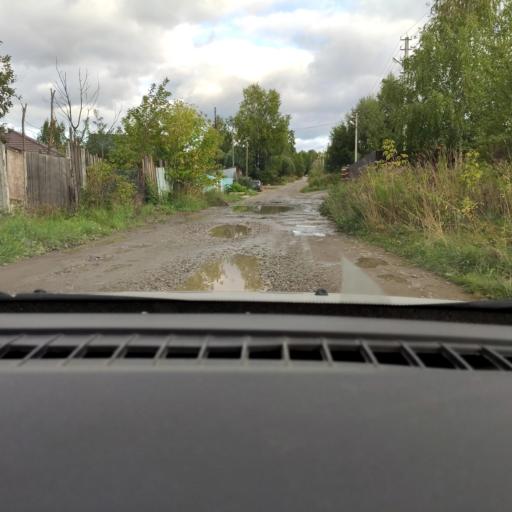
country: RU
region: Perm
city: Perm
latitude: 58.1132
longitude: 56.3943
